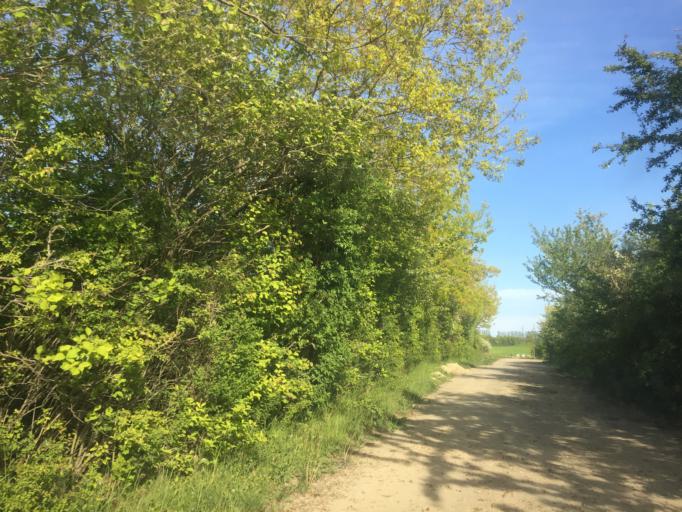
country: DK
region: Capital Region
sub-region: Hoje-Taastrup Kommune
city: Flong
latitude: 55.6466
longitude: 12.2073
